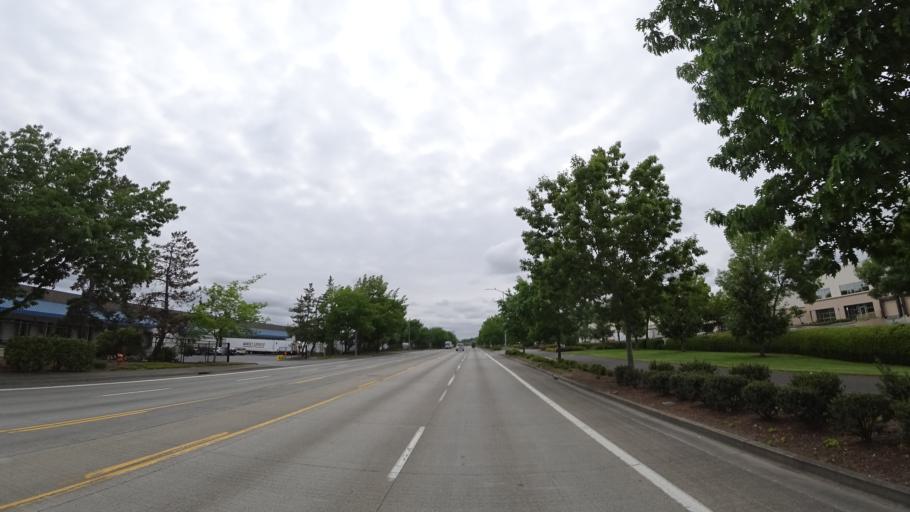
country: US
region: Washington
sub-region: Clark County
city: Vancouver
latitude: 45.6270
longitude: -122.7395
